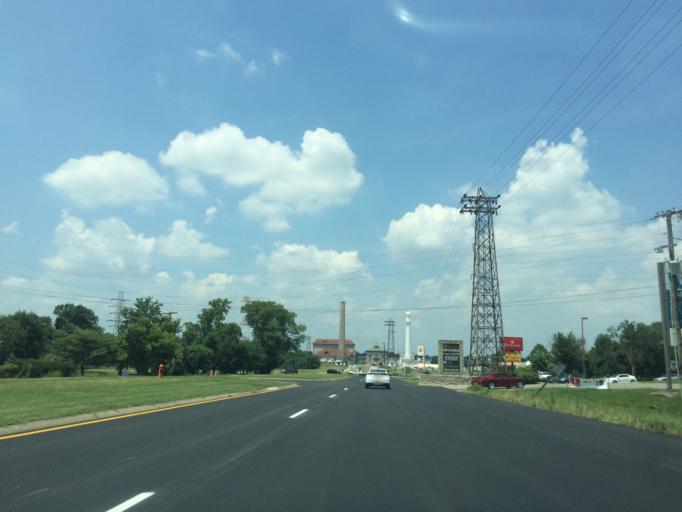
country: US
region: Indiana
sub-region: Clark County
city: Oak Park
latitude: 38.2758
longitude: -85.6978
